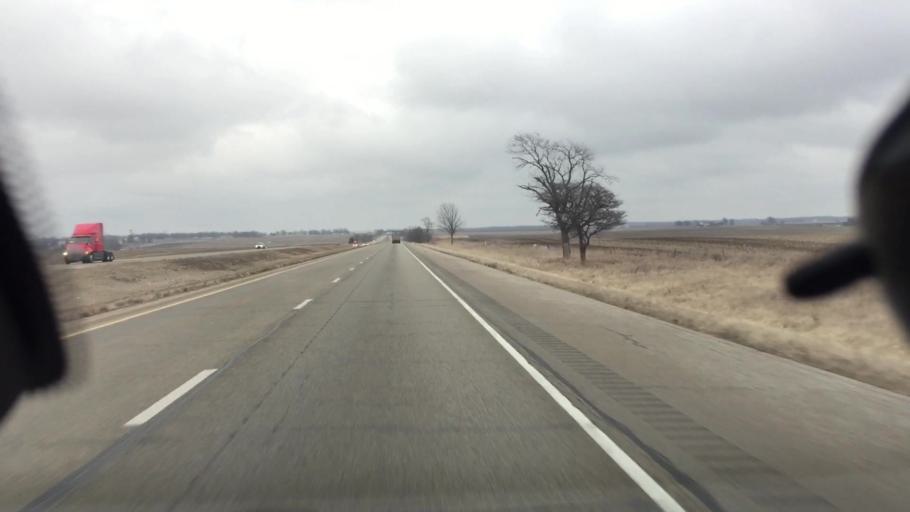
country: US
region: Illinois
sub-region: Tazewell County
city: Mackinaw
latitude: 40.6222
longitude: -89.3714
